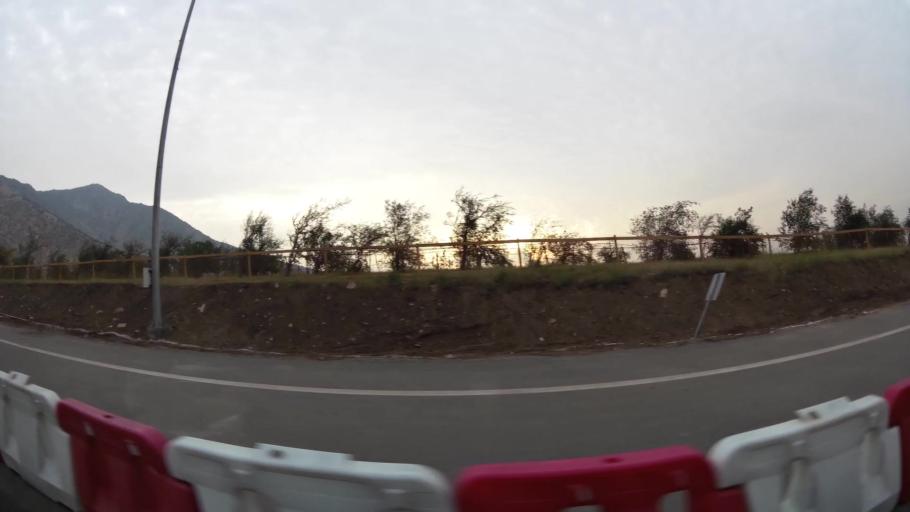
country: CL
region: Santiago Metropolitan
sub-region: Provincia de Chacabuco
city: Chicureo Abajo
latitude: -33.3311
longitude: -70.6282
